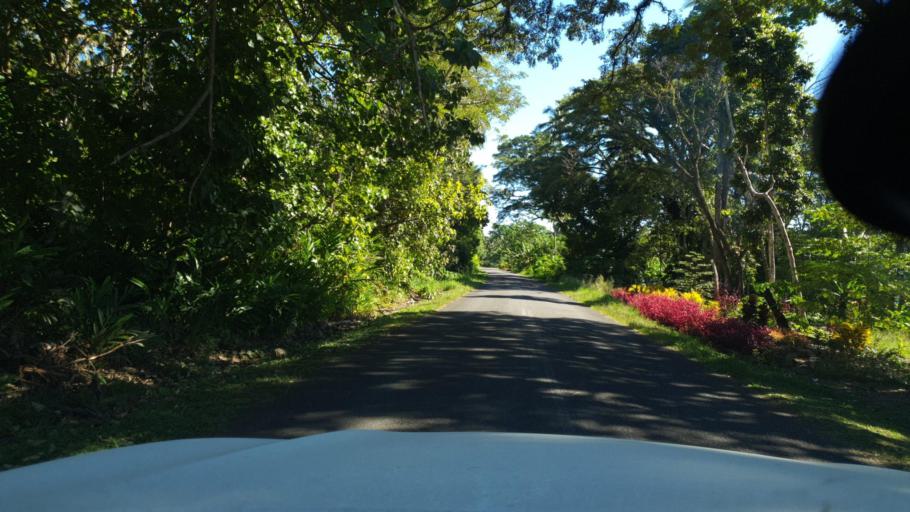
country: SB
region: Guadalcanal
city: Honiara
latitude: -9.3136
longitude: 159.7964
